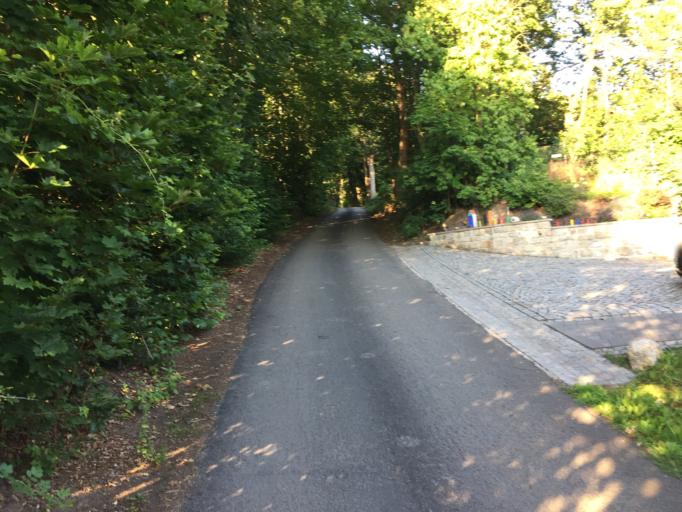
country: DE
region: Thuringia
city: Schmalkalden
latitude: 50.7239
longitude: 10.4584
